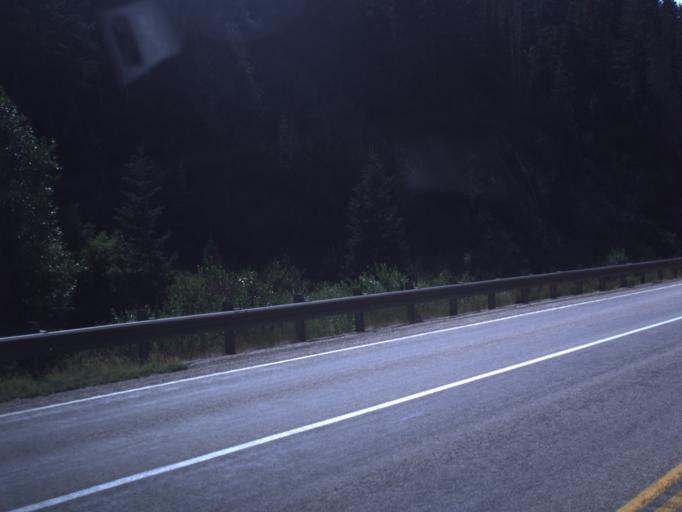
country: US
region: Utah
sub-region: Wasatch County
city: Heber
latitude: 40.3543
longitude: -111.2778
